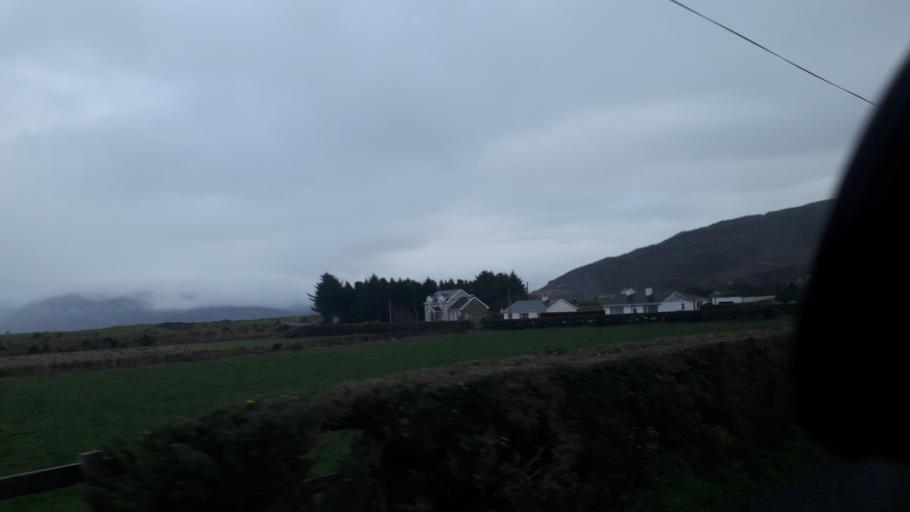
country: IE
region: Ulster
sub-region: County Donegal
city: Ramelton
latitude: 55.1879
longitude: -7.6195
